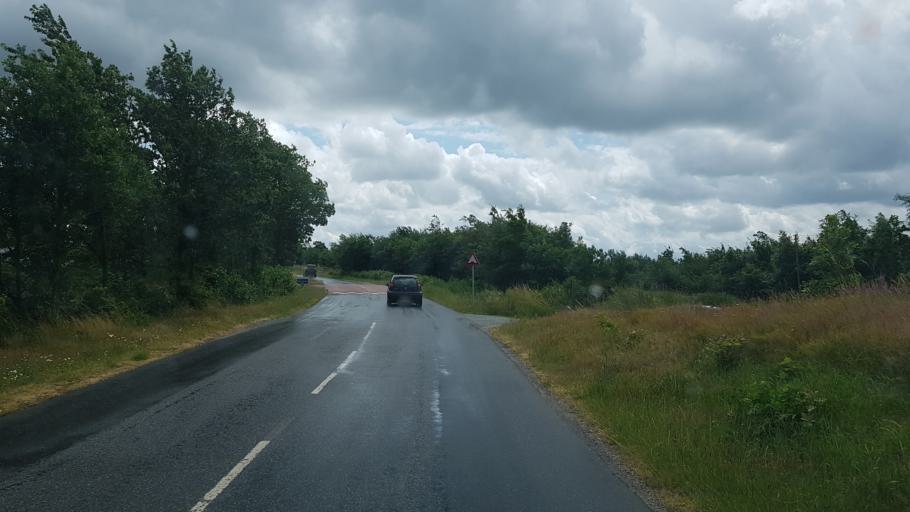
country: DK
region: South Denmark
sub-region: Kolding Kommune
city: Lunderskov
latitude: 55.4712
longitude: 9.2895
